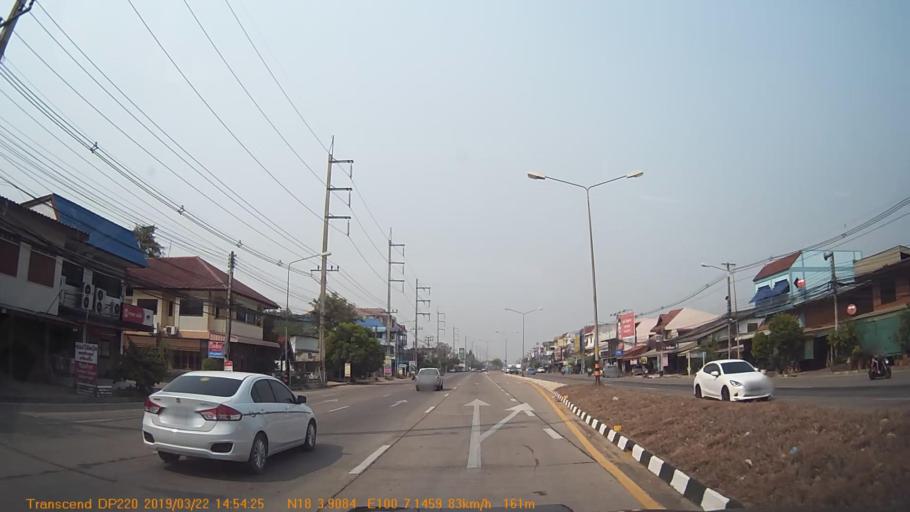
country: TH
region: Phrae
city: Sung Men
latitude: 18.0656
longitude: 100.1192
